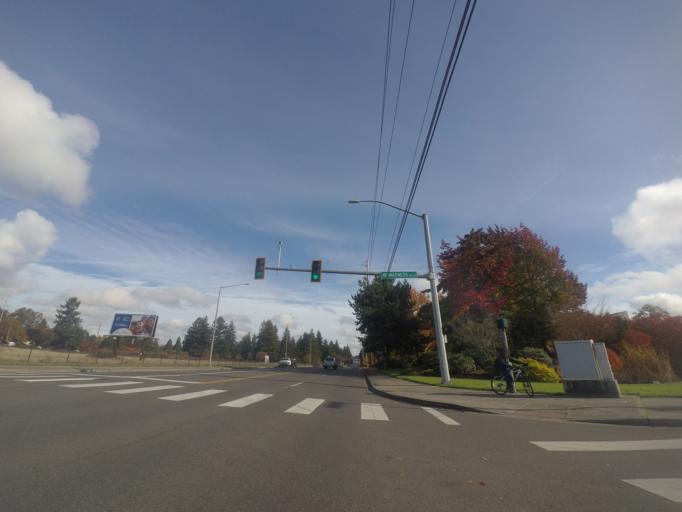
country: US
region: Washington
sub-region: Pierce County
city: Lakewood
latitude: 47.1764
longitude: -122.5003
